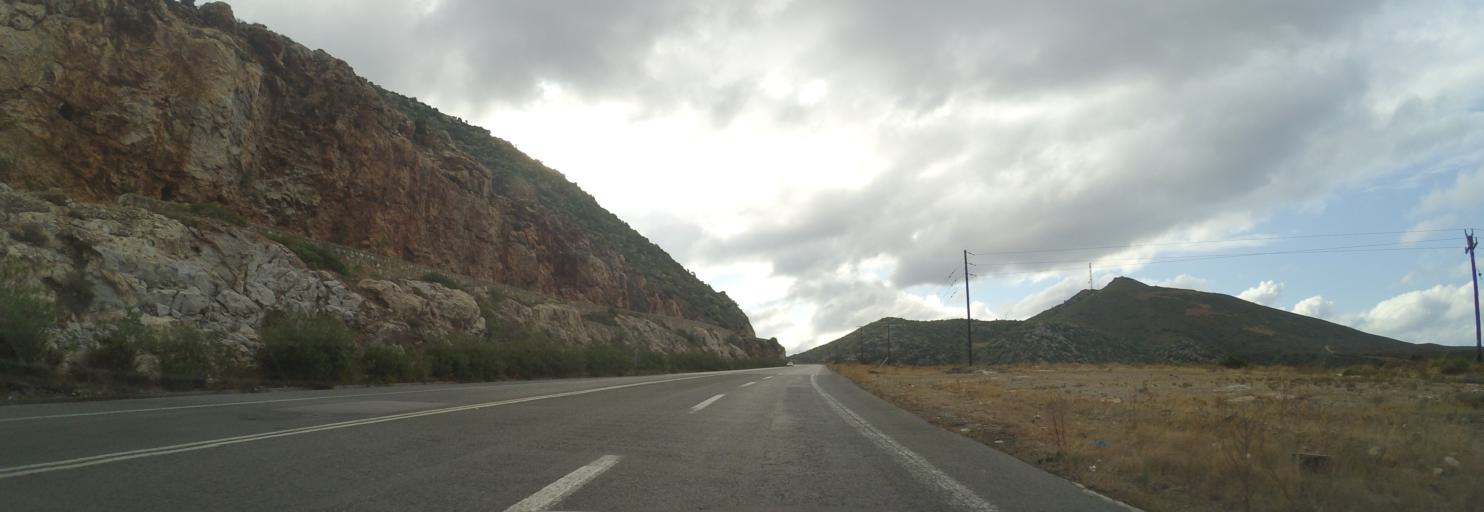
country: GR
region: Crete
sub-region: Nomos Rethymnis
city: Perama
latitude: 35.4078
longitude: 24.7663
